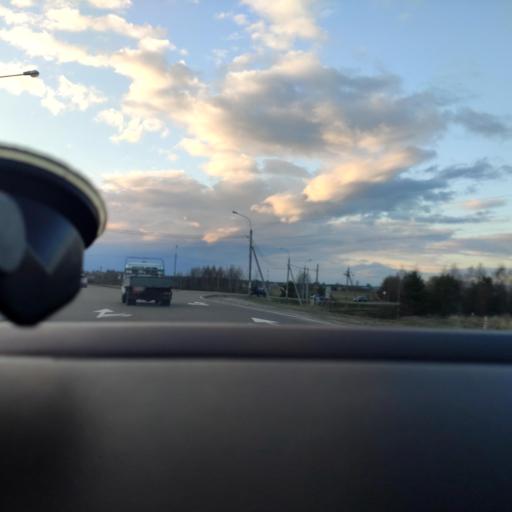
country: RU
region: Moskovskaya
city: Yegor'yevsk
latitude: 55.3879
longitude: 39.0823
